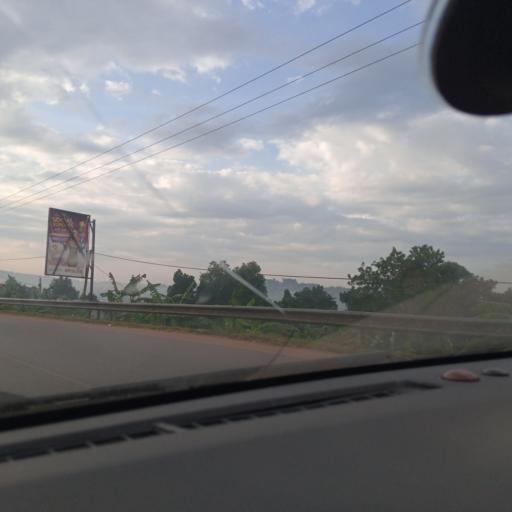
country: UG
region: Central Region
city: Masaka
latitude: -0.3396
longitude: 31.7043
